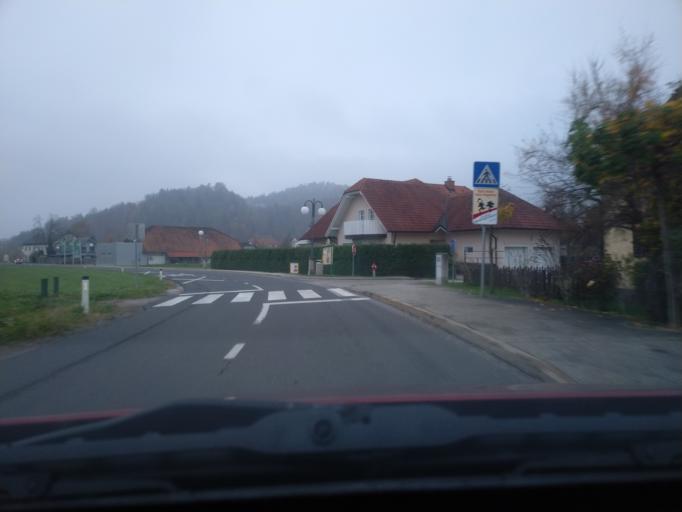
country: SI
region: Kungota
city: Zgornja Kungota
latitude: 46.6406
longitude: 15.6130
